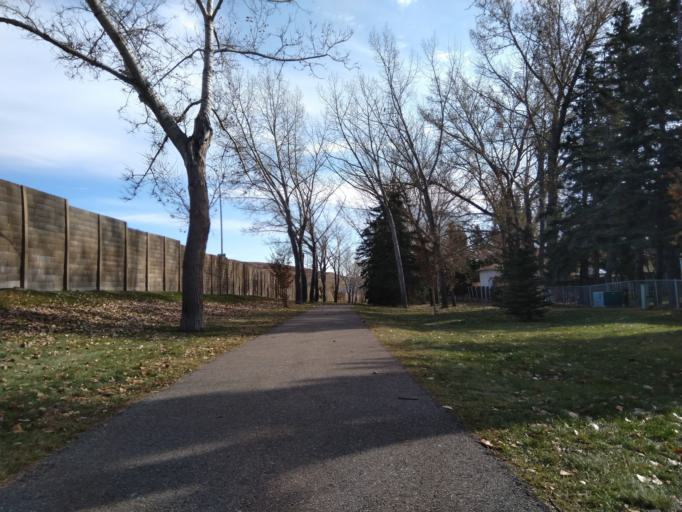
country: CA
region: Alberta
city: Calgary
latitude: 51.1055
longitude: -114.1323
